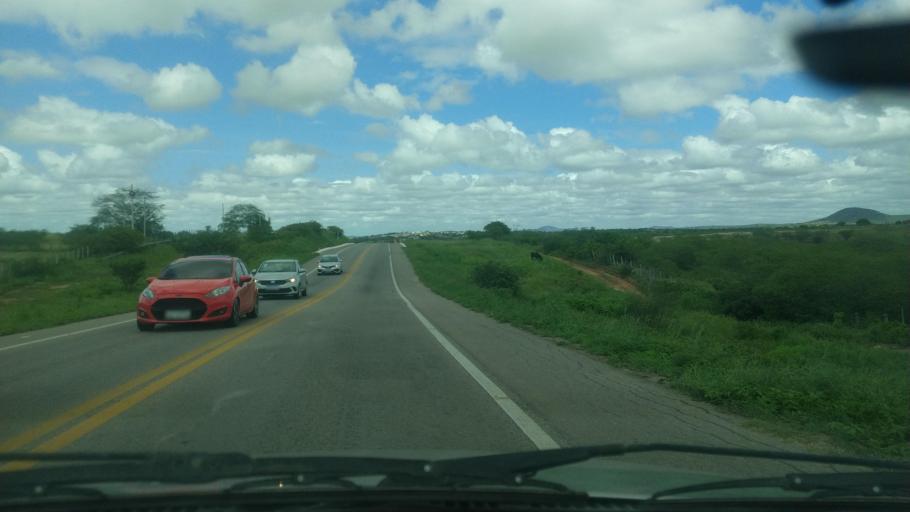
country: BR
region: Rio Grande do Norte
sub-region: Tangara
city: Tangara
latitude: -6.1817
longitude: -35.7726
